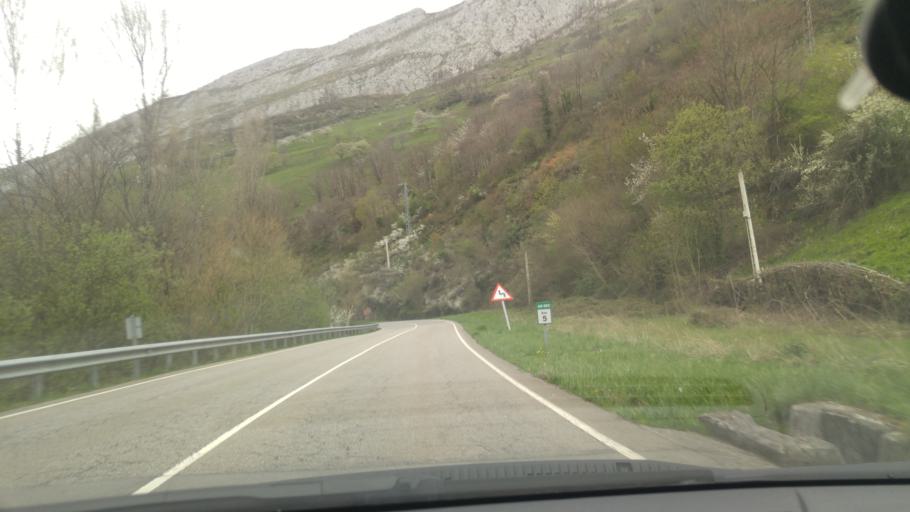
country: ES
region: Asturias
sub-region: Province of Asturias
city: Rio Aller
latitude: 43.1372
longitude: -5.5726
